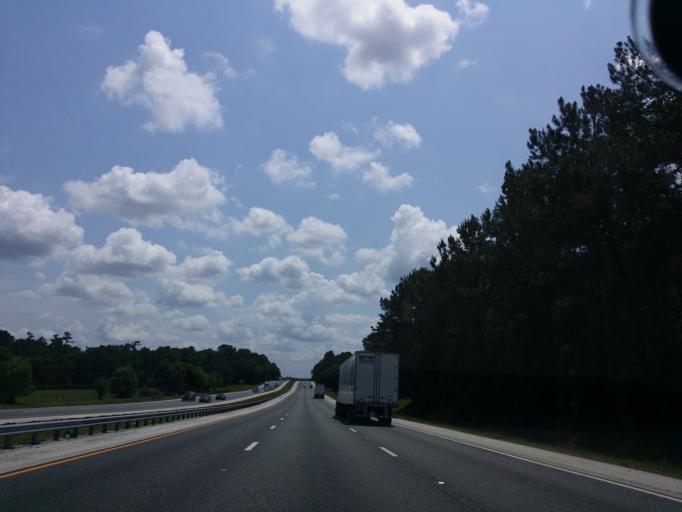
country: US
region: Florida
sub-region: Marion County
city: Citra
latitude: 29.3813
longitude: -82.2334
